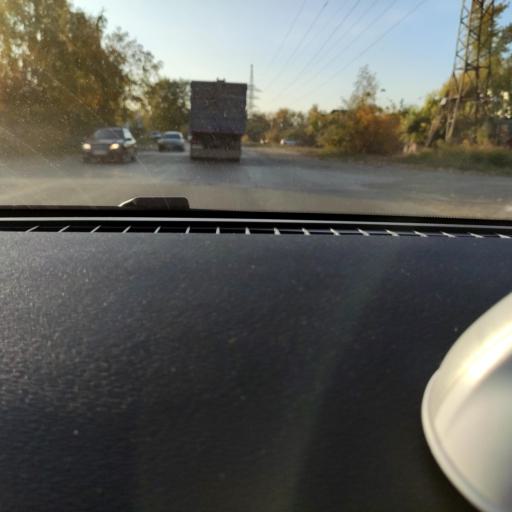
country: RU
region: Samara
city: Samara
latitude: 53.1333
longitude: 50.1277
